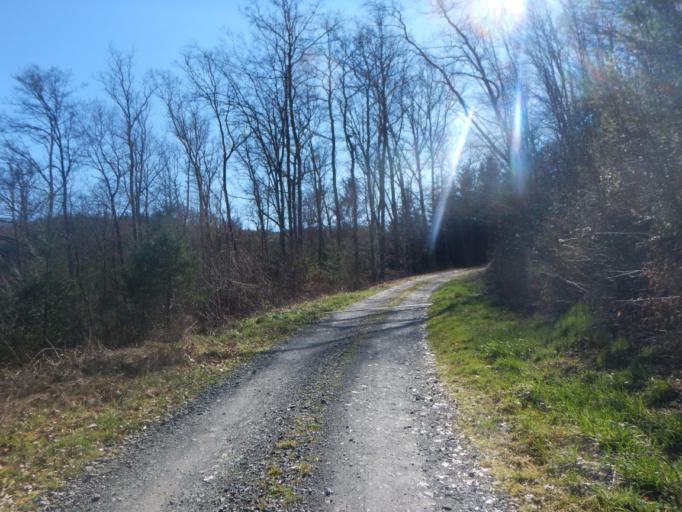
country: LU
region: Diekirch
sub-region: Canton de Wiltz
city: Eschweiler
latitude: 49.9879
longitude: 5.9622
